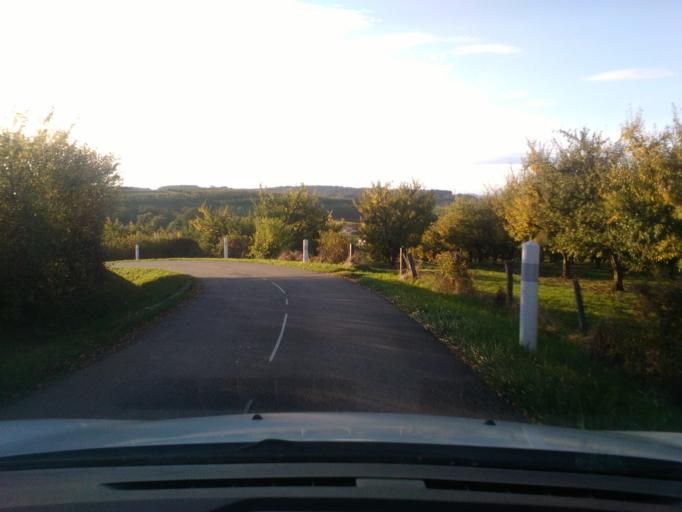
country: FR
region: Lorraine
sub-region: Departement des Vosges
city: Vincey
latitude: 48.3261
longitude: 6.3037
